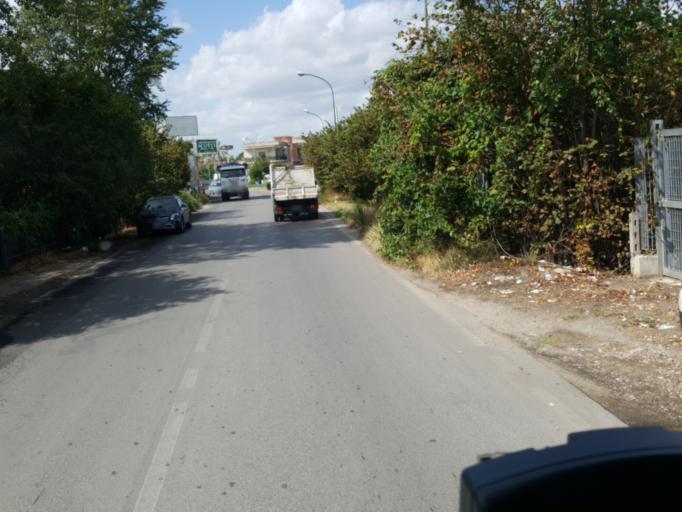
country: IT
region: Campania
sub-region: Provincia di Napoli
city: Nola
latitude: 40.9167
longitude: 14.5273
